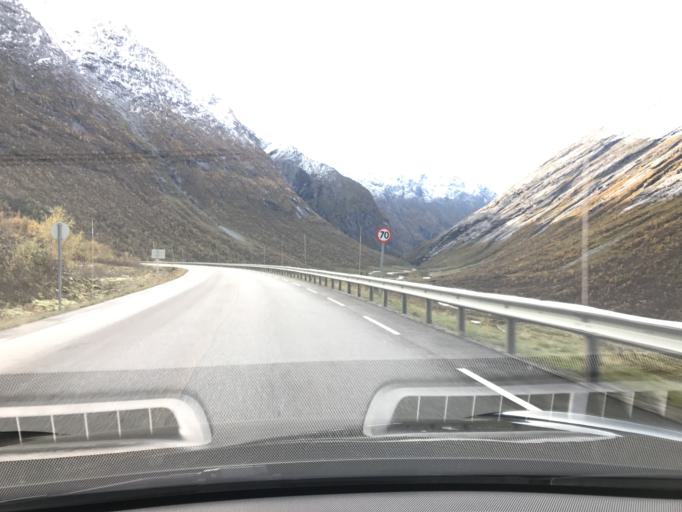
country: NO
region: More og Romsdal
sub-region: Norddal
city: Valldal
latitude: 61.9703
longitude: 7.2461
